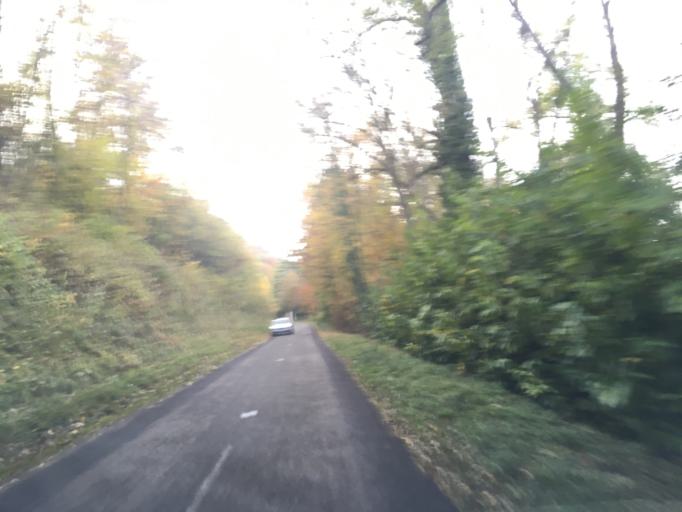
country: FR
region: Haute-Normandie
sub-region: Departement de l'Eure
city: Heudreville-sur-Eure
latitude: 49.1101
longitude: 1.2139
